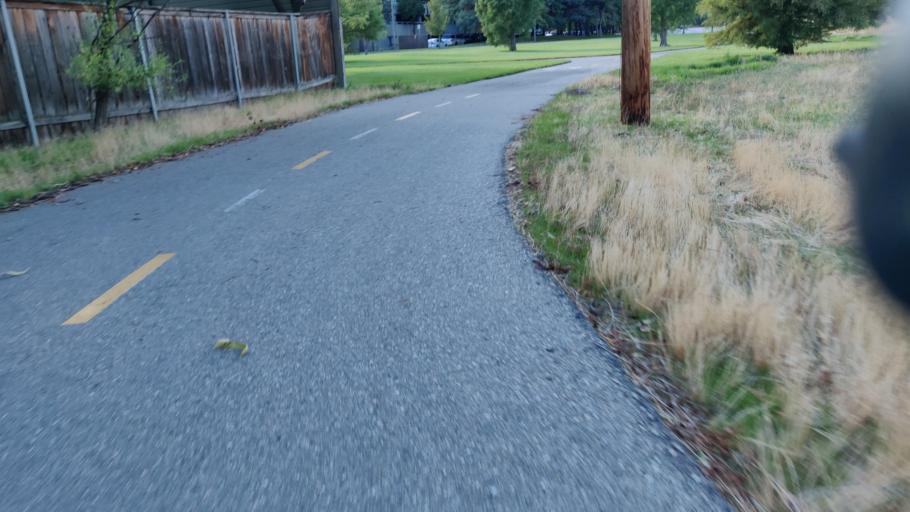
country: US
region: Idaho
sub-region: Ada County
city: Boise
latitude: 43.6049
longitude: -116.1865
